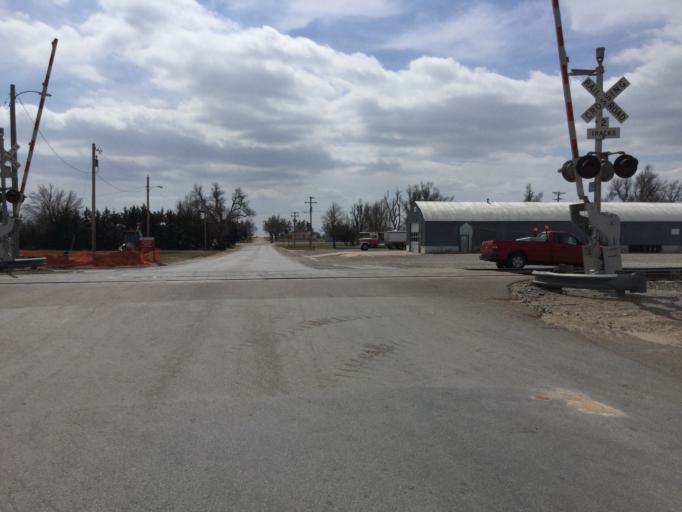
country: US
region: Kansas
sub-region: Kiowa County
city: Greensburg
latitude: 37.6154
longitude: -99.1062
